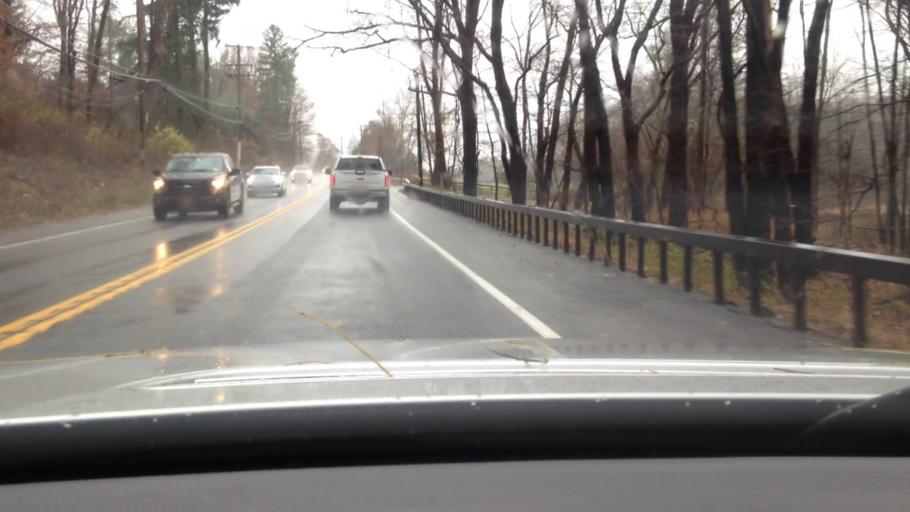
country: US
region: New York
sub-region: Orange County
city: Highland Falls
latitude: 41.3470
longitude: -73.9270
